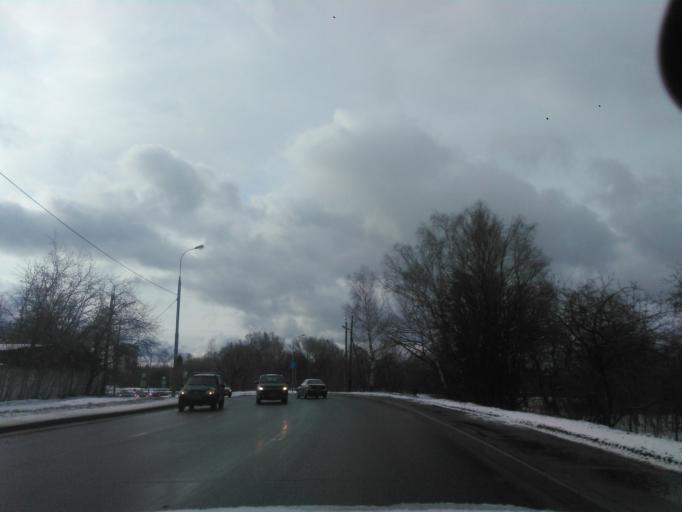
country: RU
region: Moscow
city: Zelenograd
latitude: 55.9719
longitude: 37.1820
